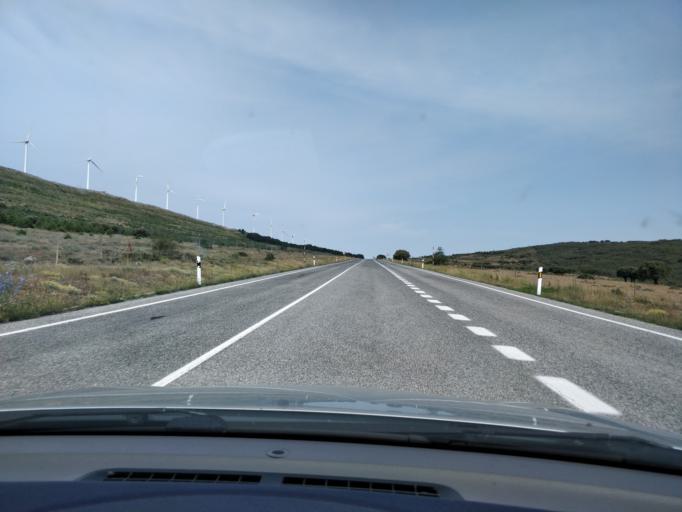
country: ES
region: Castille and Leon
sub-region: Provincia de Burgos
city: Medina de Pomar
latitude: 42.9257
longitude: -3.6340
